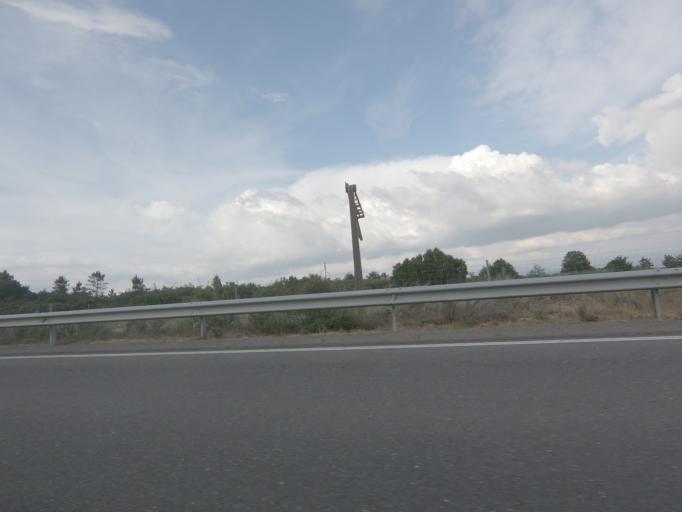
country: ES
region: Galicia
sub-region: Provincia de Ourense
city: Ambia
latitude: 42.1574
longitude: -7.7585
